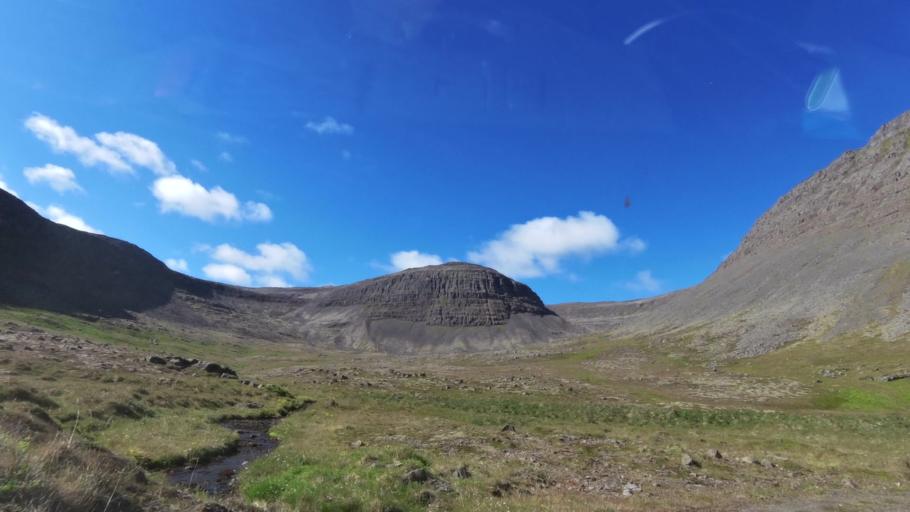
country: IS
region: West
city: Olafsvik
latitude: 65.6243
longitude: -23.8953
